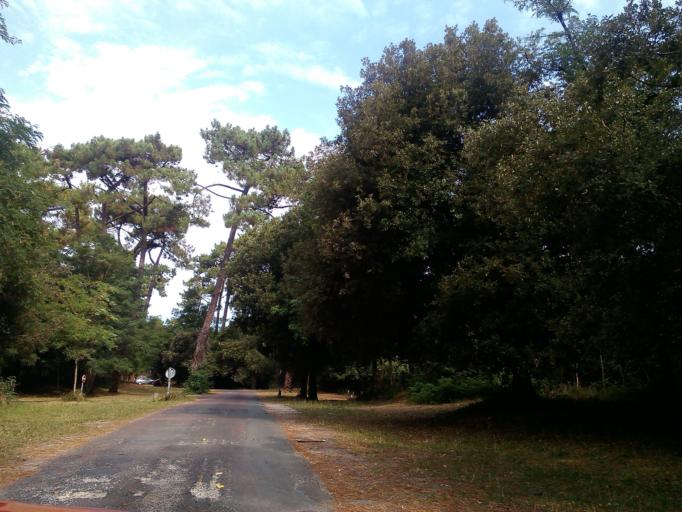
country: FR
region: Poitou-Charentes
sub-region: Departement de la Charente-Maritime
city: Saint-Trojan-les-Bains
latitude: 45.7910
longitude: -1.2050
